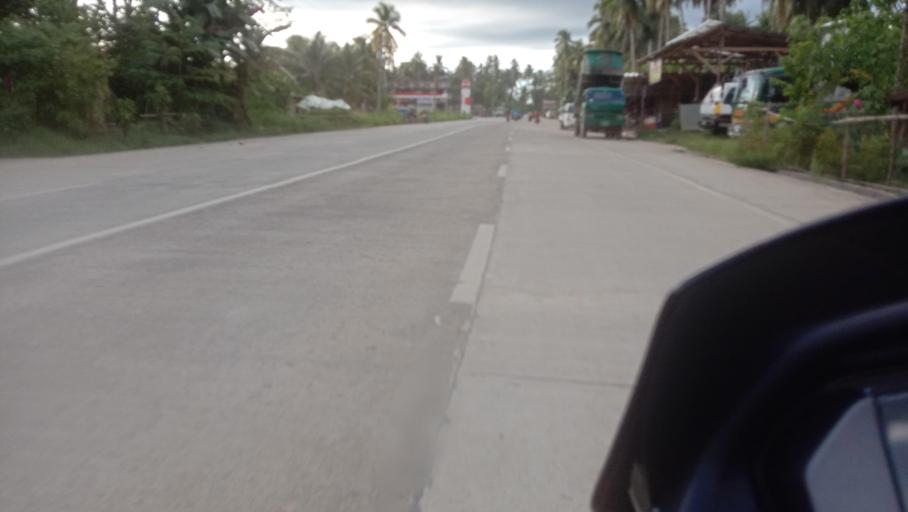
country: PH
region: Caraga
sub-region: Province of Surigao del Sur
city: Barobo
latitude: 8.5201
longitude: 126.1214
